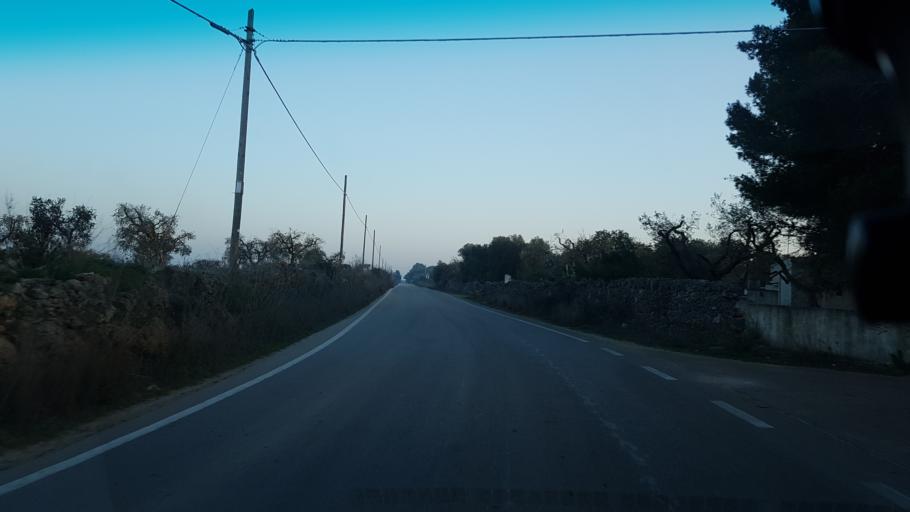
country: IT
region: Apulia
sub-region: Provincia di Brindisi
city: San Vito dei Normanni
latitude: 40.6484
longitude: 17.7756
